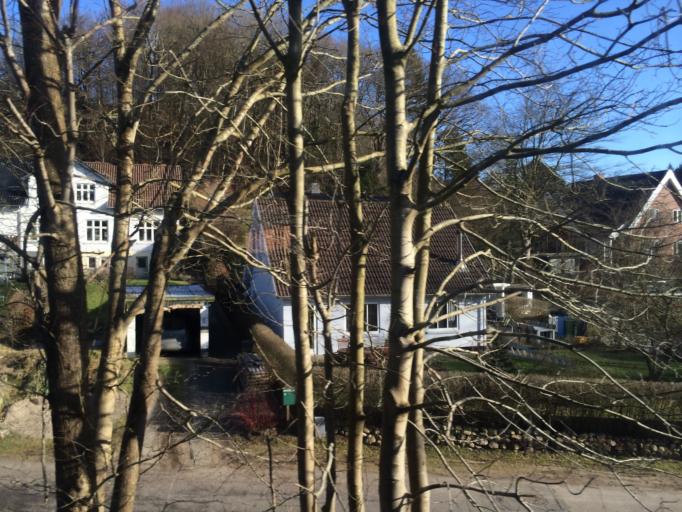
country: DK
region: South Denmark
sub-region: Vejle Kommune
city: Vejle
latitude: 55.7446
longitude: 9.5386
